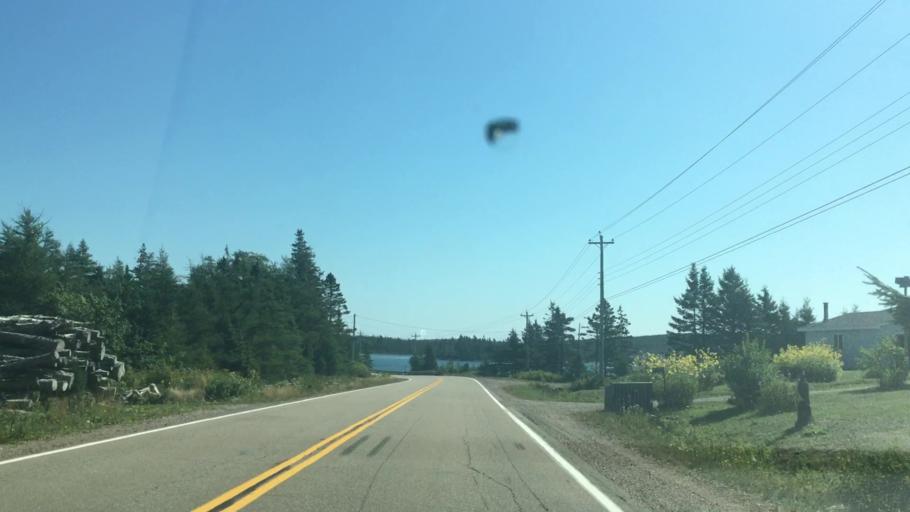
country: CA
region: Nova Scotia
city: Antigonish
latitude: 45.0235
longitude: -62.0211
